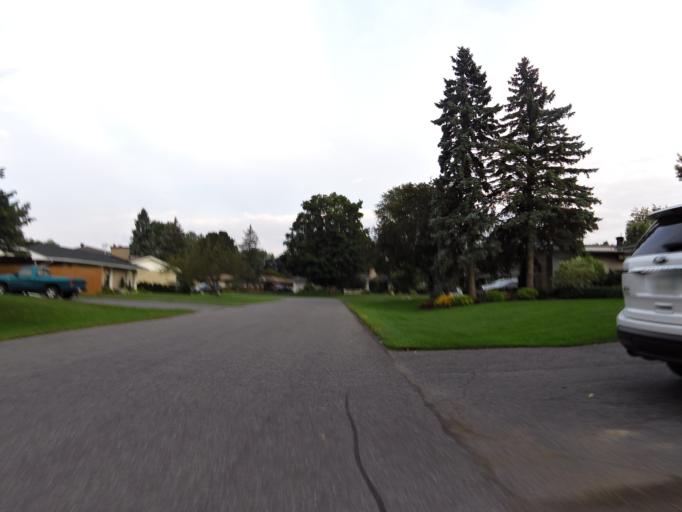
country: CA
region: Ontario
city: Bells Corners
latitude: 45.3215
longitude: -75.8200
